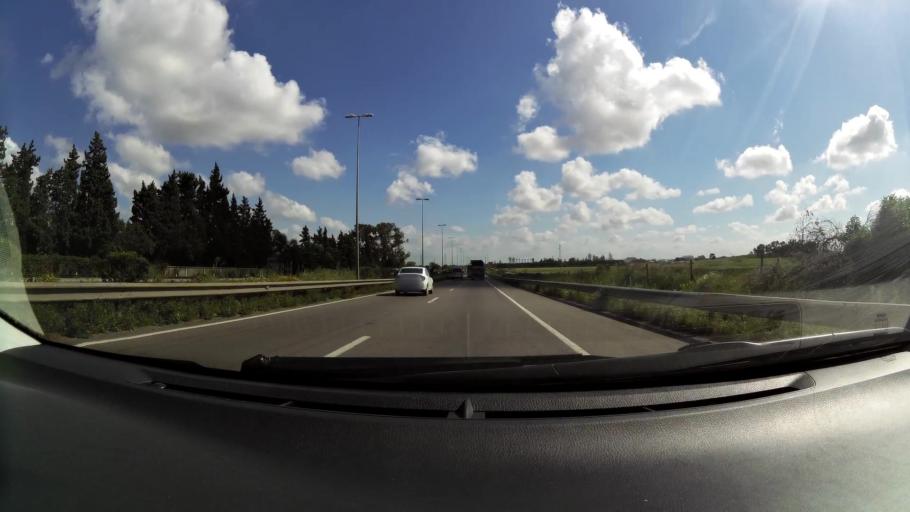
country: MA
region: Grand Casablanca
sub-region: Nouaceur
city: Bouskoura
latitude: 33.4630
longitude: -7.6335
